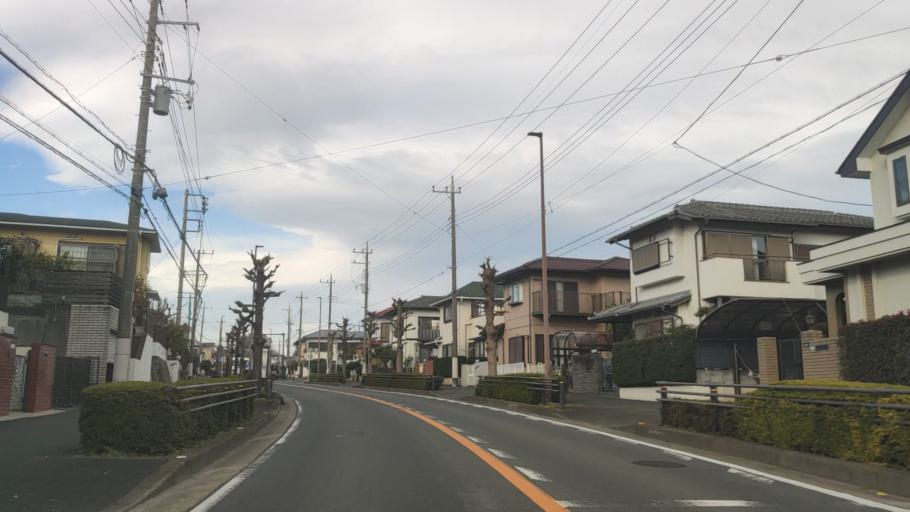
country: JP
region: Kanagawa
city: Atsugi
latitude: 35.4418
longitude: 139.4027
